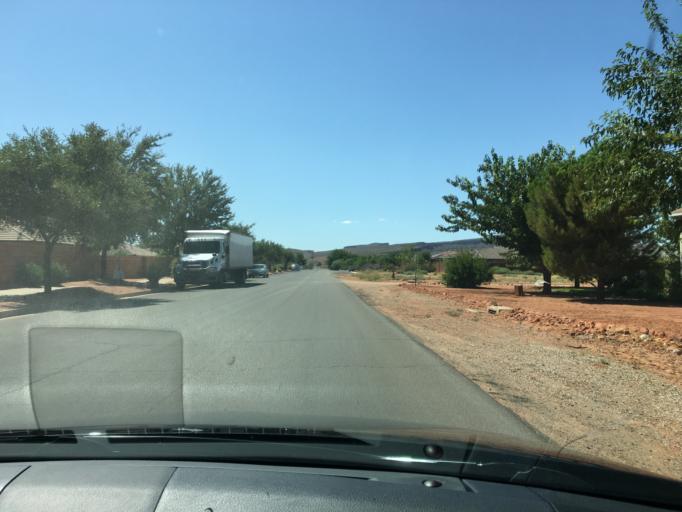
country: US
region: Utah
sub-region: Washington County
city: Ivins
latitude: 37.1635
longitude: -113.6887
